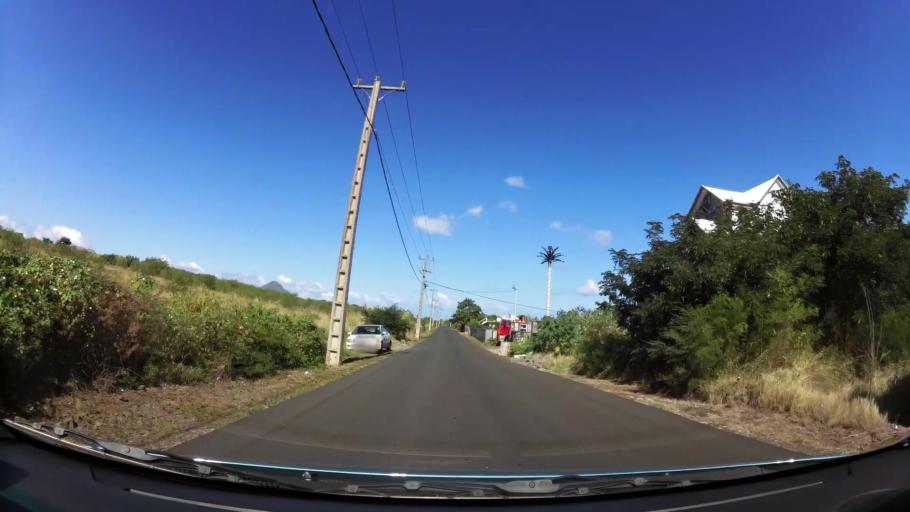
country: MU
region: Black River
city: Flic en Flac
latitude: -20.2695
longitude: 57.3769
